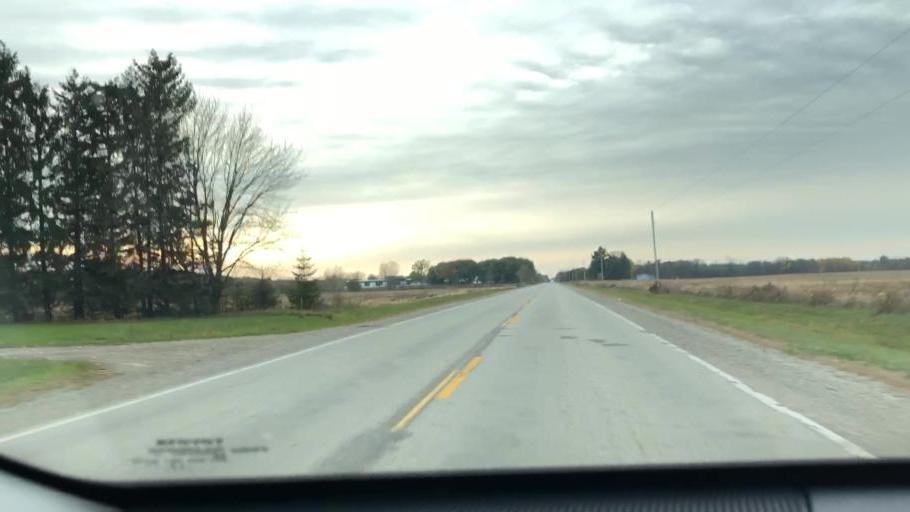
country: US
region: Wisconsin
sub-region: Brown County
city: Oneida
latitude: 44.4442
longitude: -88.1955
